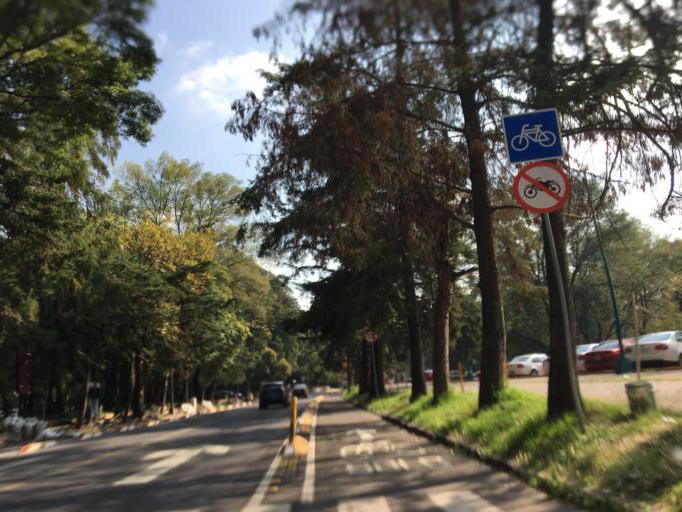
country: MX
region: Mexico City
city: Miguel Hidalgo
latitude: 19.4274
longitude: -99.1858
